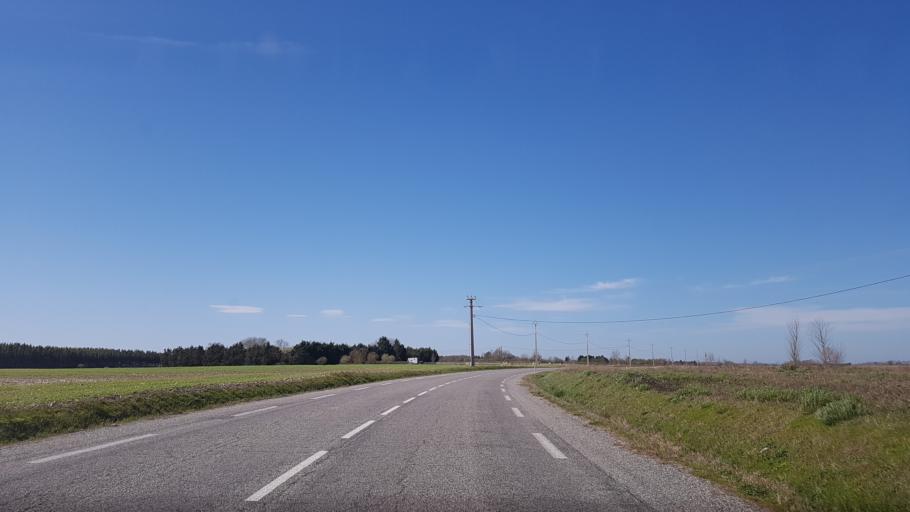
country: FR
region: Midi-Pyrenees
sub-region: Departement de l'Ariege
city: Mazeres
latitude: 43.2276
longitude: 1.6799
